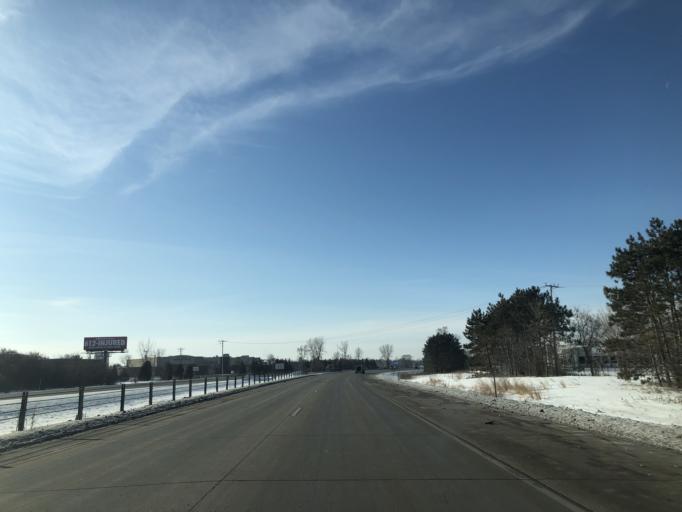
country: US
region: Minnesota
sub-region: Anoka County
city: Lino Lakes
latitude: 45.1752
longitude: -93.1217
